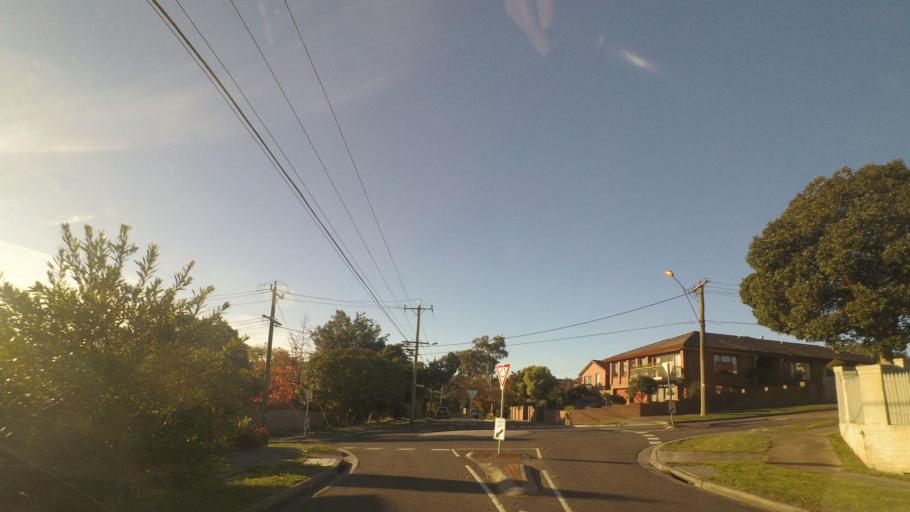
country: AU
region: Victoria
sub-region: Manningham
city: Doncaster East
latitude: -37.7958
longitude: 145.1559
